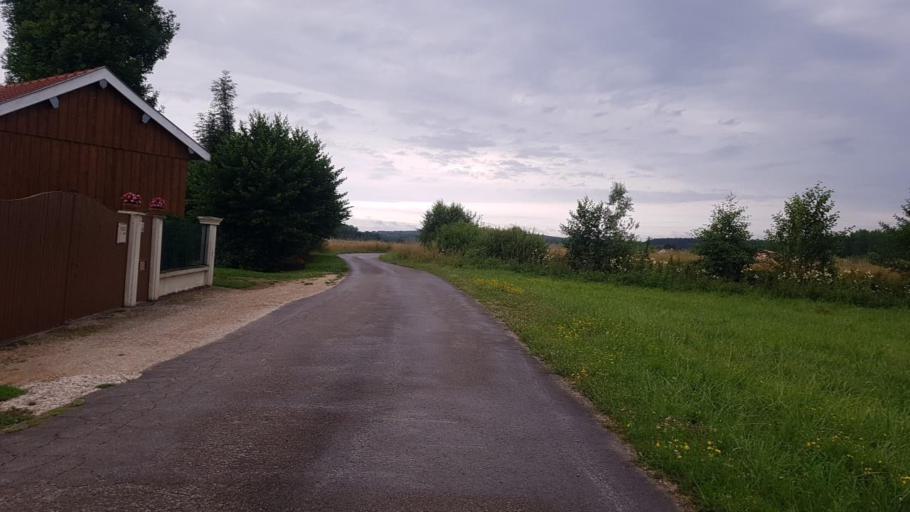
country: FR
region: Champagne-Ardenne
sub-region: Departement de la Marne
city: Vitry-le-Francois
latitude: 48.7398
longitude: 4.6607
